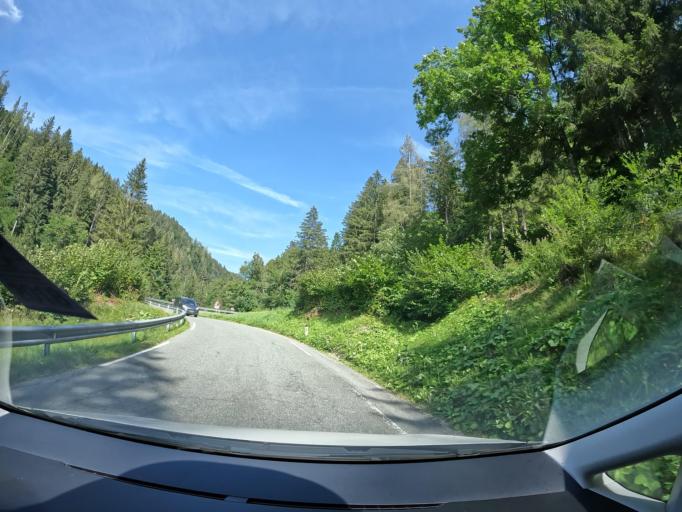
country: SI
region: Jesenice
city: Koroska Bela
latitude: 46.4977
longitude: 14.1000
